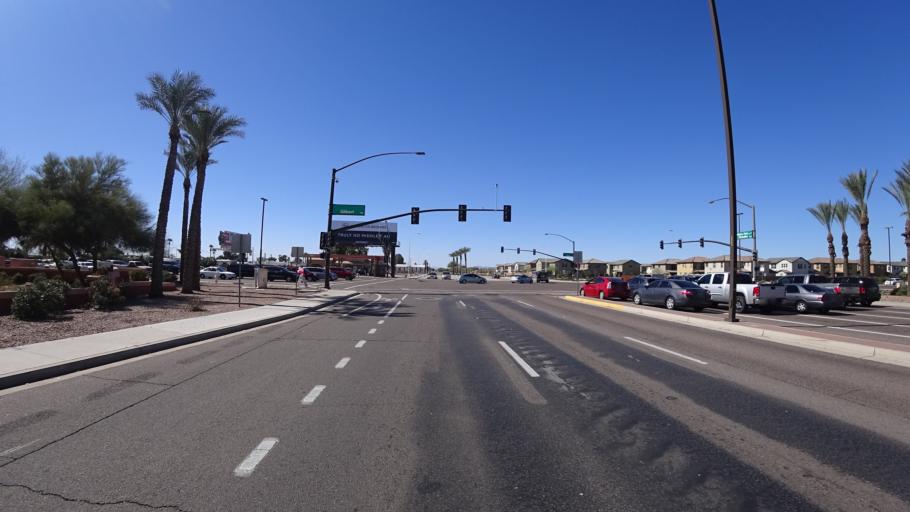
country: US
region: Arizona
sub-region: Maricopa County
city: Gilbert
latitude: 33.3063
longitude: -111.7893
